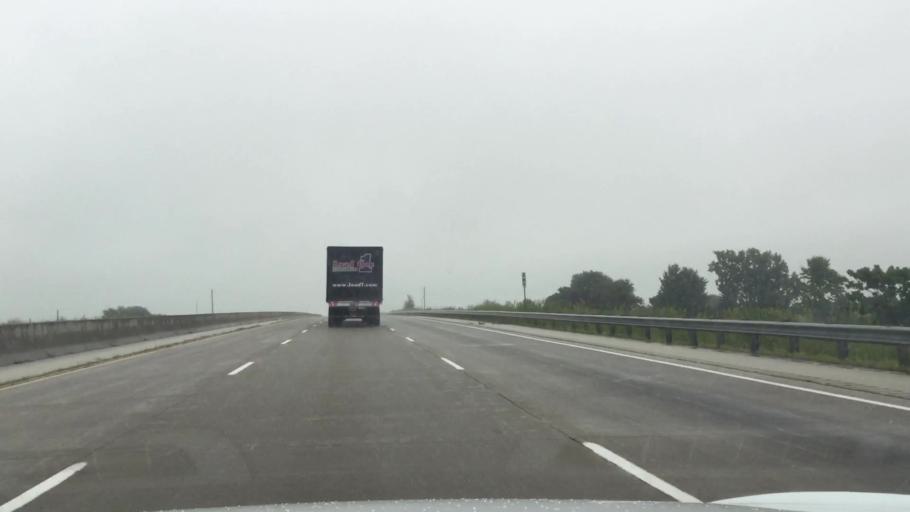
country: US
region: Michigan
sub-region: Wayne County
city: Grosse Pointe Farms
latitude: 42.2332
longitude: -82.6403
